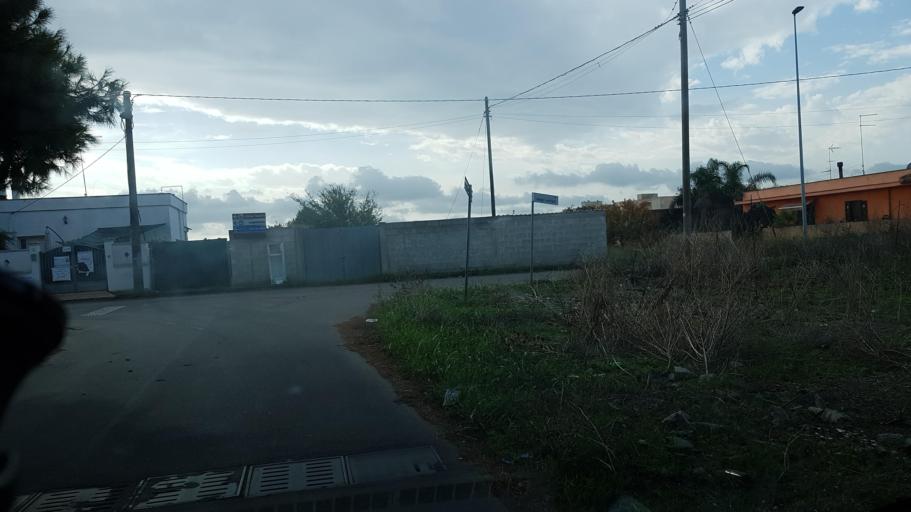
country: IT
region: Apulia
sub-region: Provincia di Brindisi
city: San Pietro Vernotico
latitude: 40.4854
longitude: 18.0053
